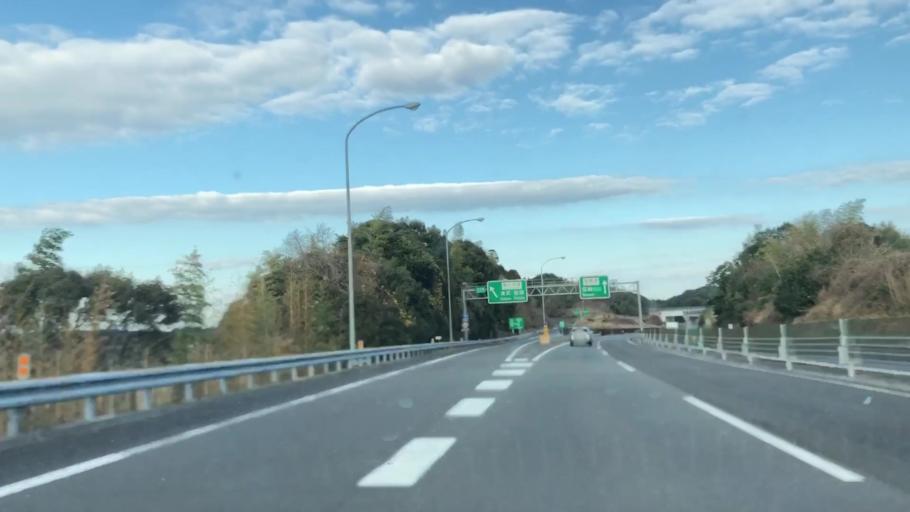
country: JP
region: Miyazaki
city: Miyazaki-shi
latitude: 31.8460
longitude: 131.3536
